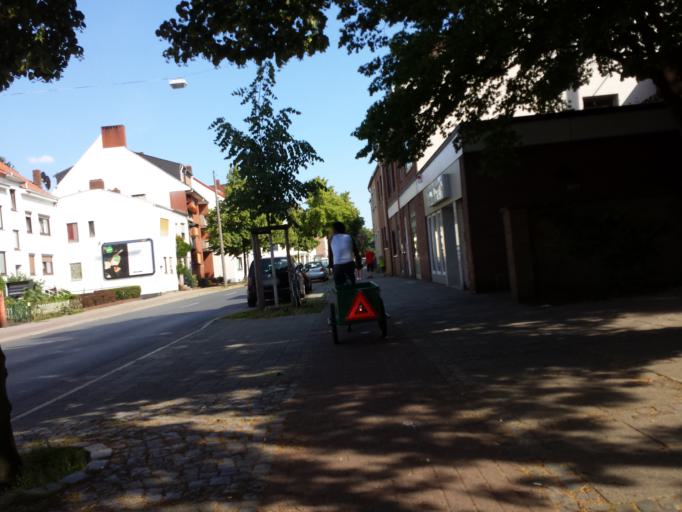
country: DE
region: Bremen
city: Bremen
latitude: 53.0871
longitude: 8.7621
